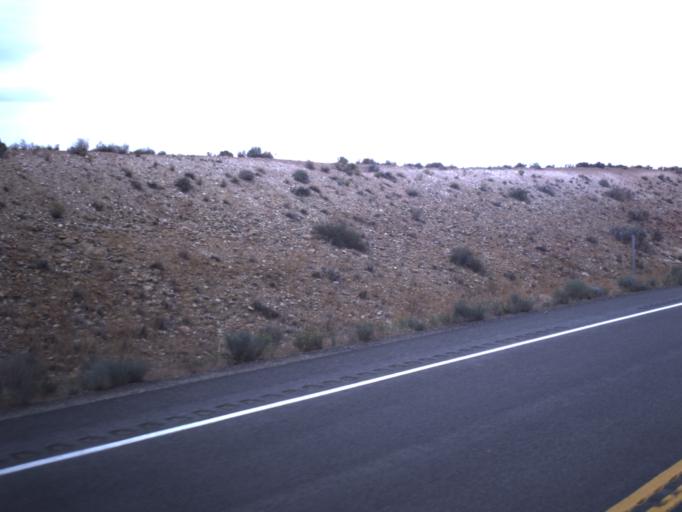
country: US
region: Utah
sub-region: Uintah County
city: Naples
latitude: 40.2728
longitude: -109.4610
